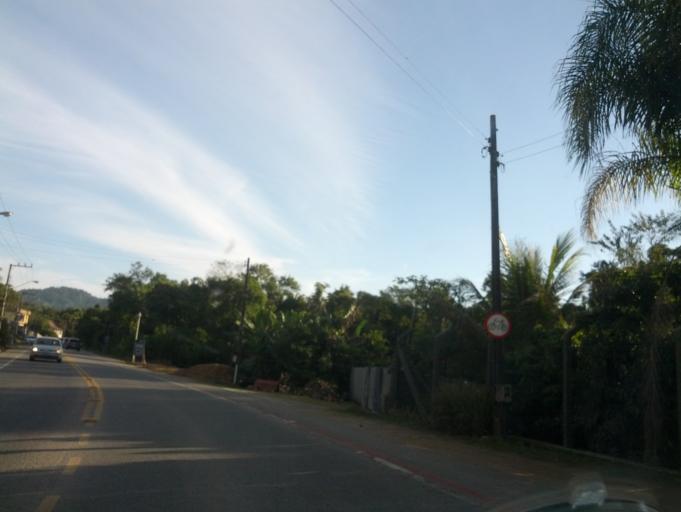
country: BR
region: Santa Catarina
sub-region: Indaial
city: Indaial
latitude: -26.8850
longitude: -49.1854
